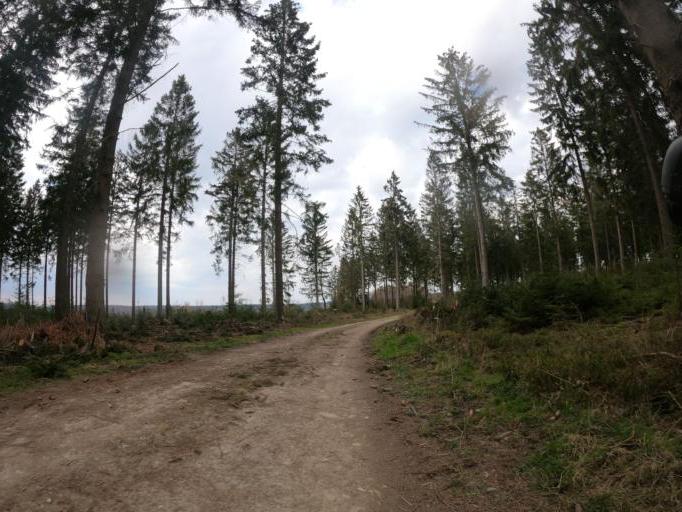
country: DE
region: North Rhine-Westphalia
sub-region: Regierungsbezirk Koln
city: Hurtgenwald
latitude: 50.7071
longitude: 6.3535
